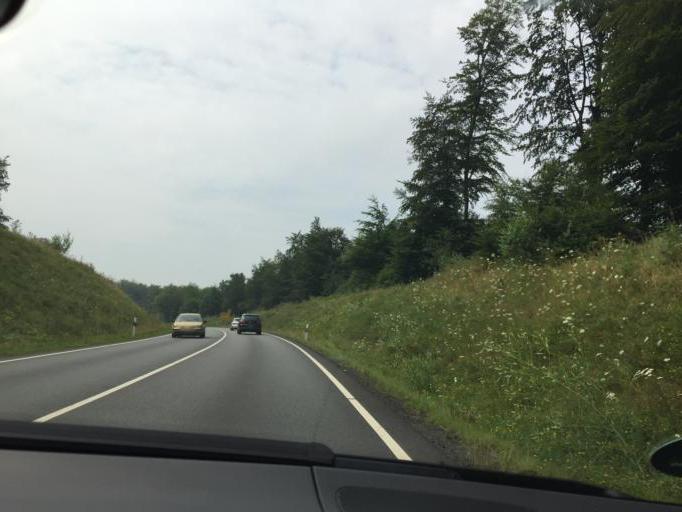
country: DE
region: Rheinland-Pfalz
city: Bonefeld
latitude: 50.5169
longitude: 7.4843
